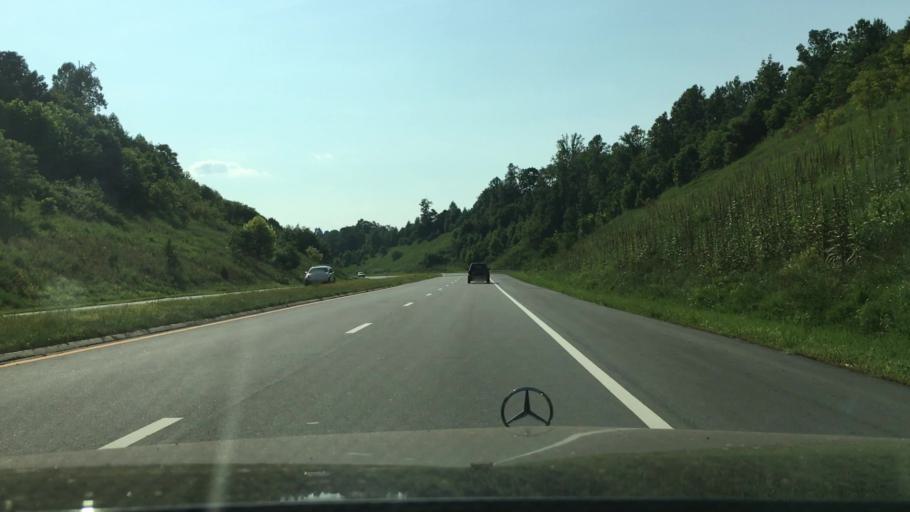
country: US
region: Virginia
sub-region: Amherst County
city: Madison Heights
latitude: 37.4128
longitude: -79.0962
